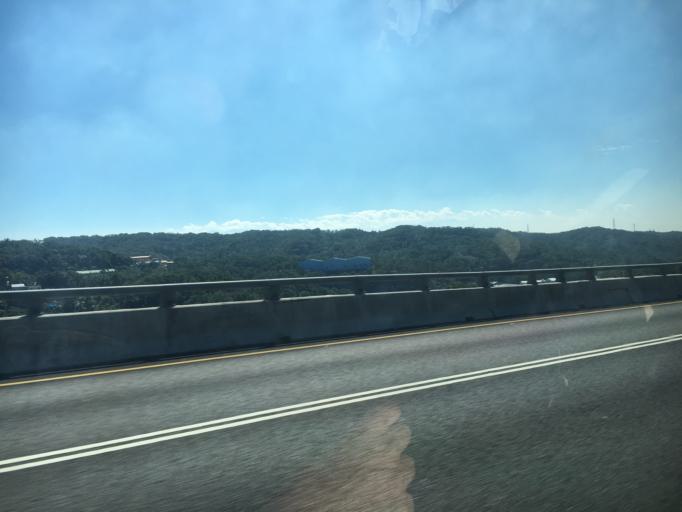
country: TW
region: Taiwan
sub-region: Taoyuan
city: Taoyuan
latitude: 25.0613
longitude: 121.3335
